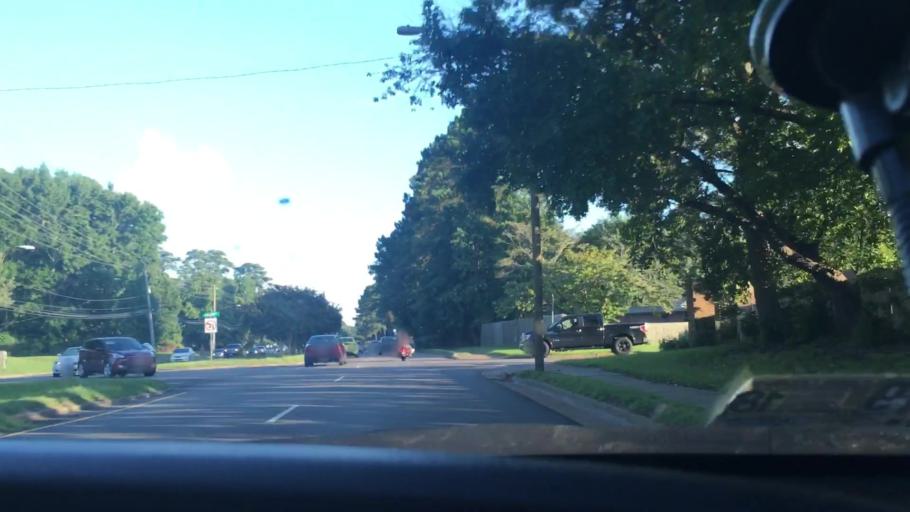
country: US
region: Virginia
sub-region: City of Norfolk
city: Norfolk
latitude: 36.8898
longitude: -76.1382
